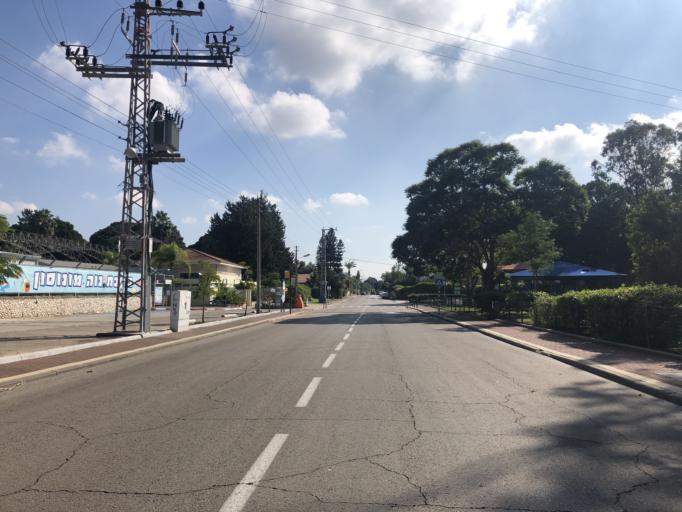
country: IL
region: Tel Aviv
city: Or Yehuda
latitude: 32.0311
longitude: 34.8739
